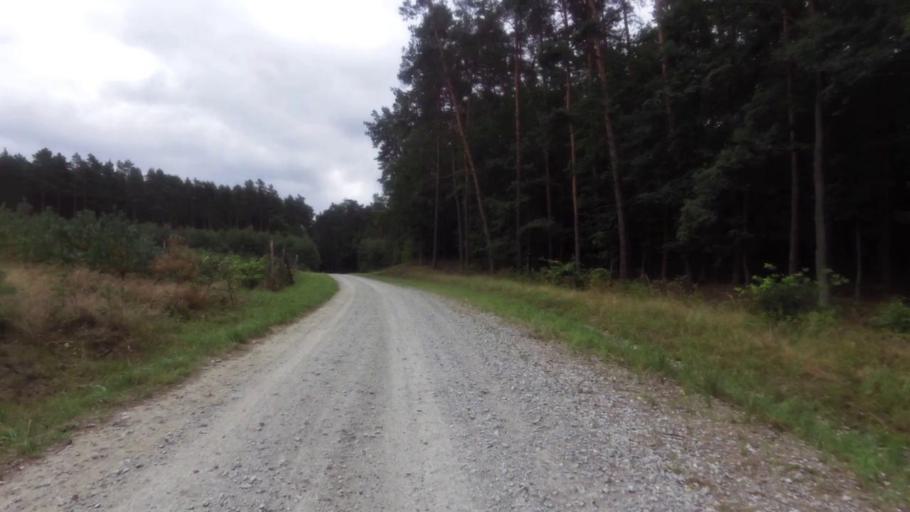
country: PL
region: Lubusz
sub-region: Powiat gorzowski
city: Kostrzyn nad Odra
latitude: 52.6519
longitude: 14.6382
